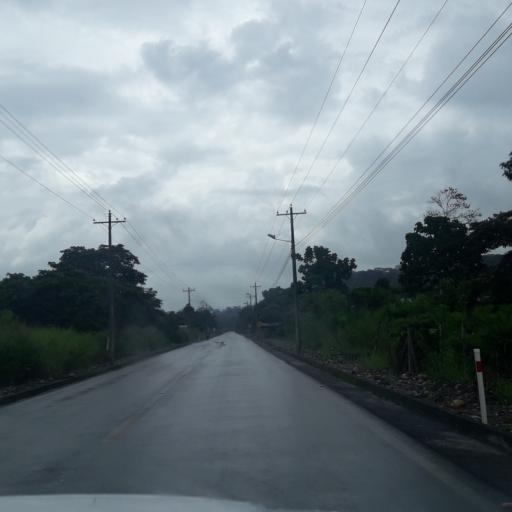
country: EC
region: Napo
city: Tena
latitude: -1.0657
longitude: -77.6435
